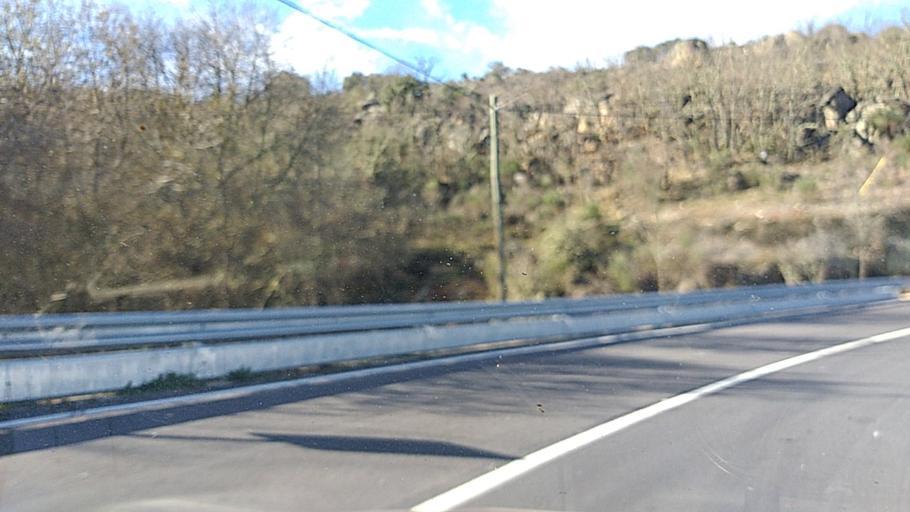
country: ES
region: Castille and Leon
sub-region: Provincia de Salamanca
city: Fuentes de Onoro
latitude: 40.6070
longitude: -6.9261
